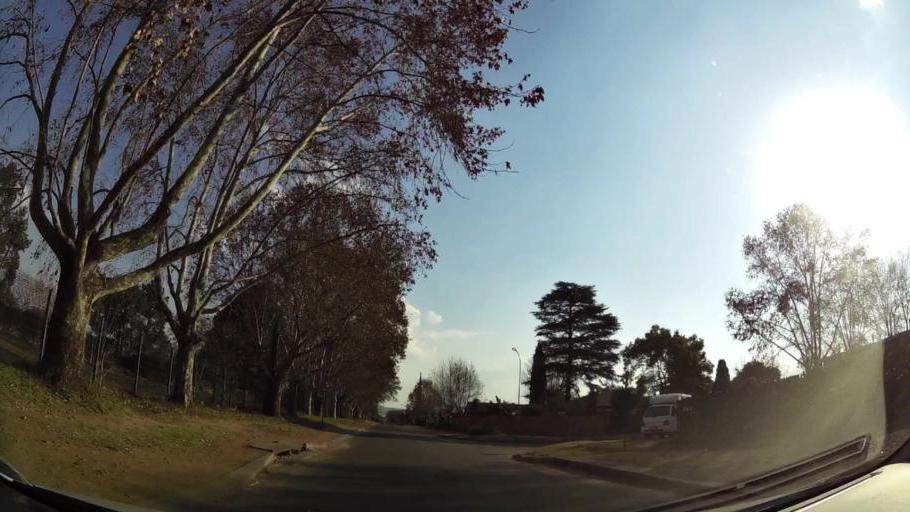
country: ZA
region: Gauteng
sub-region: Ekurhuleni Metropolitan Municipality
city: Tembisa
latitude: -25.9565
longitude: 28.2279
